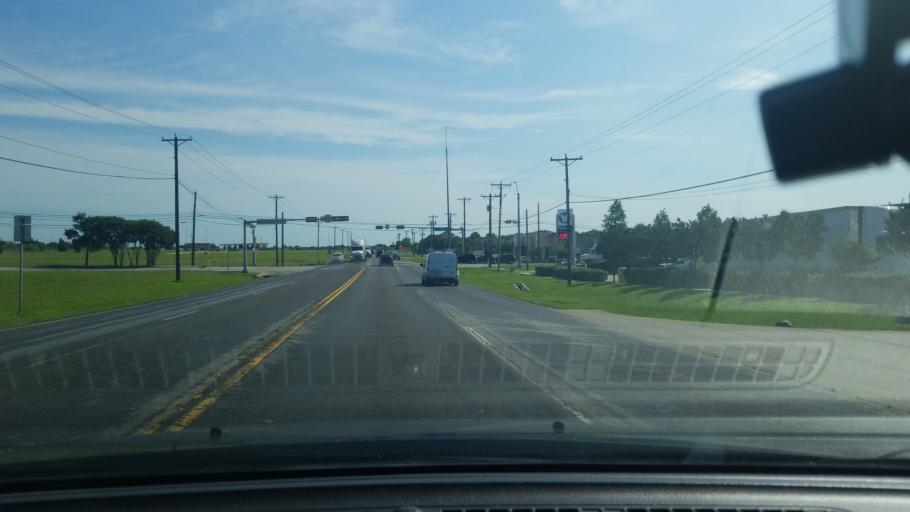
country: US
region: Texas
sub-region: Dallas County
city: Sunnyvale
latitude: 32.7787
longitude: -96.5669
